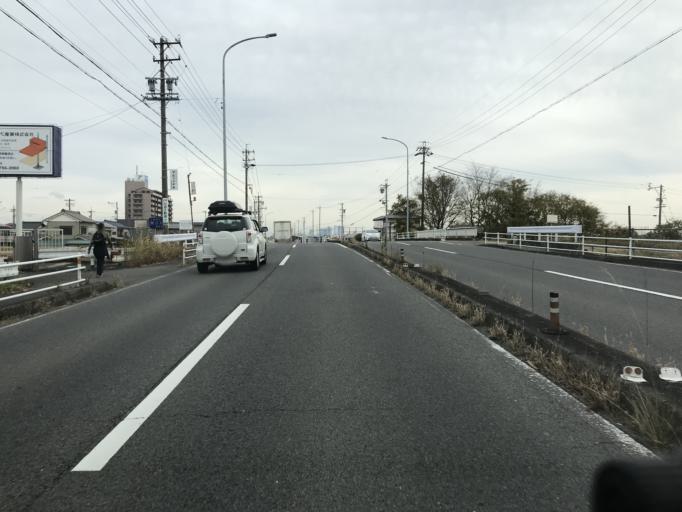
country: JP
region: Aichi
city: Kanie
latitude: 35.1850
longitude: 136.7889
